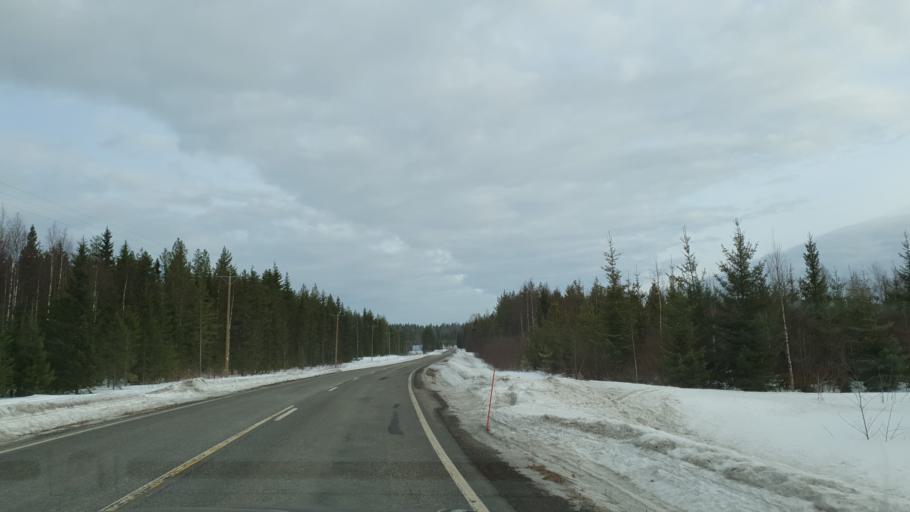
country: FI
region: Kainuu
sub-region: Kajaani
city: Vuokatti
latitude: 64.2369
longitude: 28.0554
